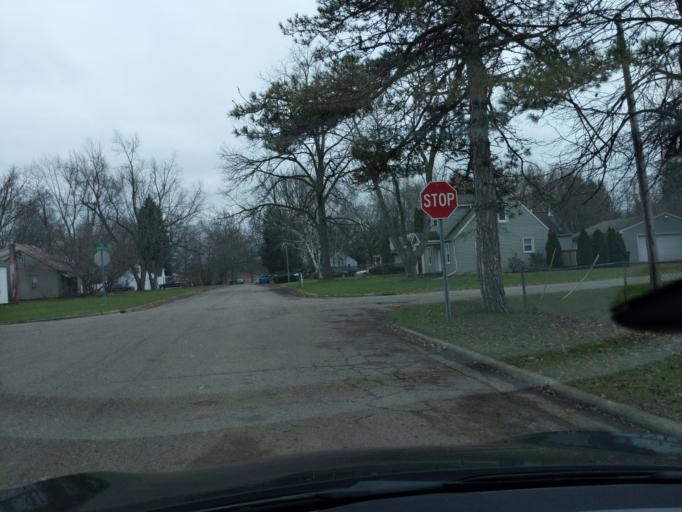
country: US
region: Michigan
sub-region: Ingham County
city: Lansing
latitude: 42.6996
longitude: -84.5872
